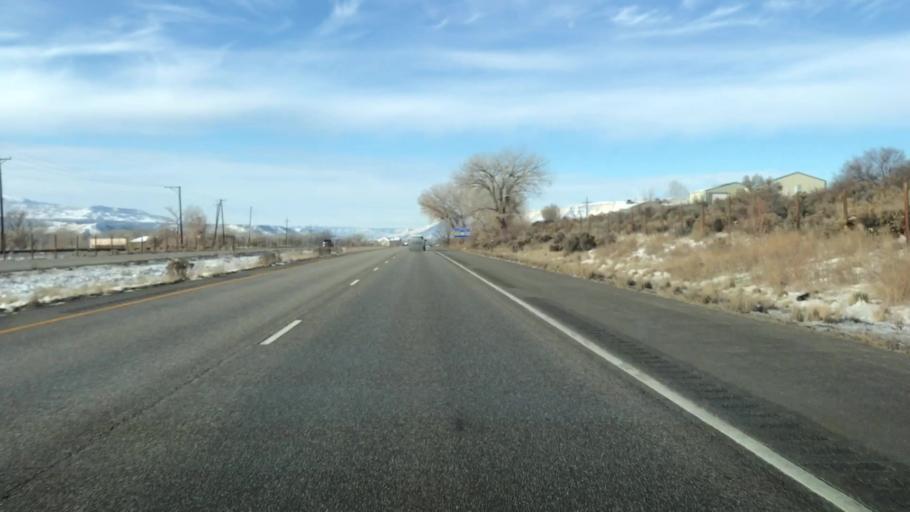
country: US
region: Colorado
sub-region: Garfield County
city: Silt
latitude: 39.5449
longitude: -107.6331
